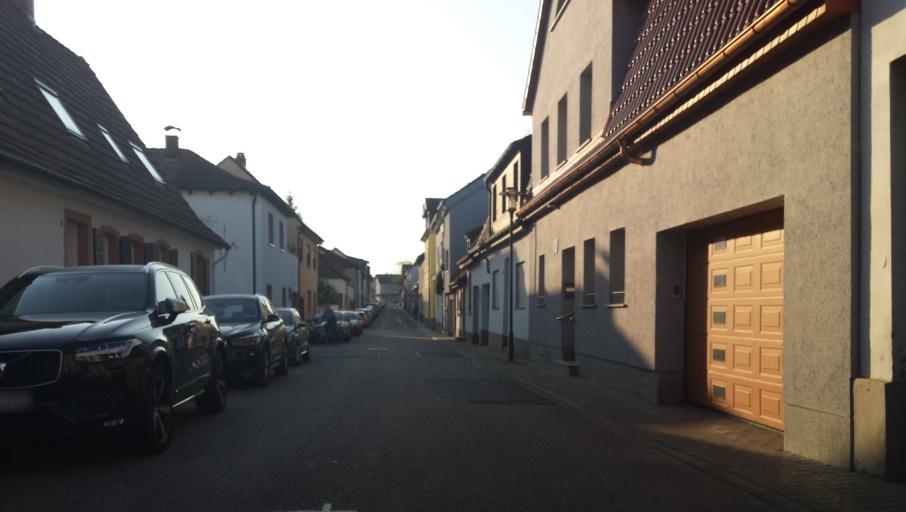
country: DE
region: Baden-Wuerttemberg
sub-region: Karlsruhe Region
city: Bruhl
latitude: 49.3930
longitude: 8.5315
